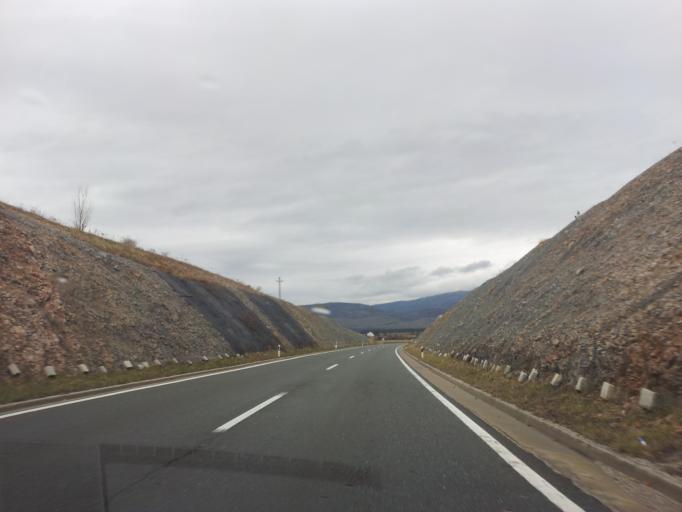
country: HR
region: Zadarska
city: Gracac
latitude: 44.5339
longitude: 15.7502
